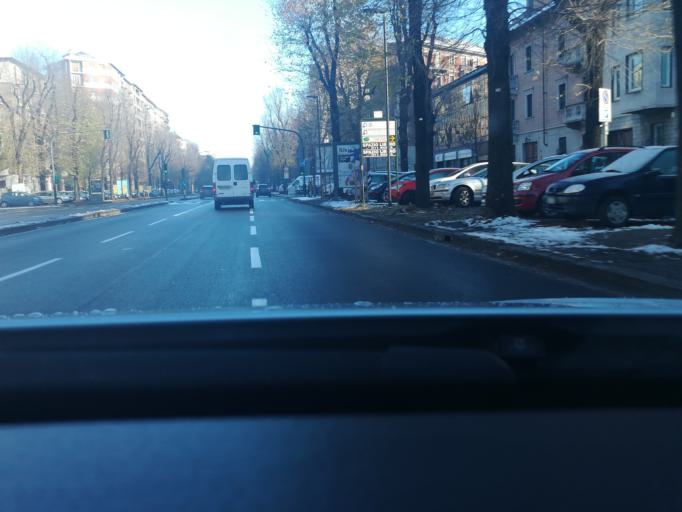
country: IT
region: Piedmont
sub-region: Provincia di Torino
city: Lesna
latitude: 45.0693
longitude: 7.6391
